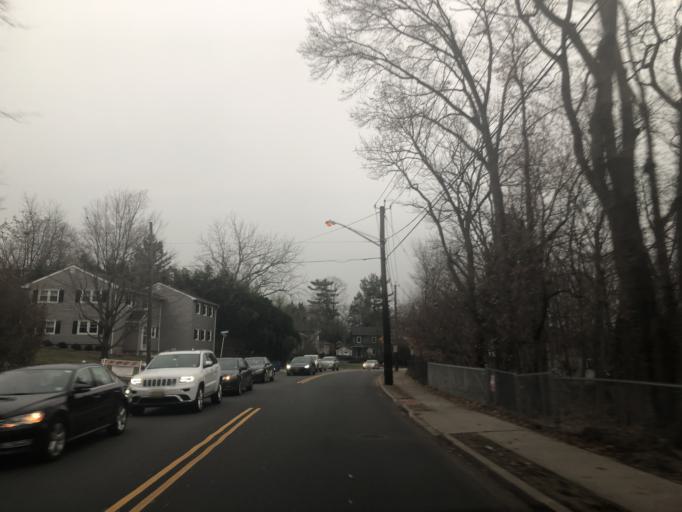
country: US
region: New Jersey
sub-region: Essex County
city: Maplewood
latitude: 40.7263
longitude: -74.2741
